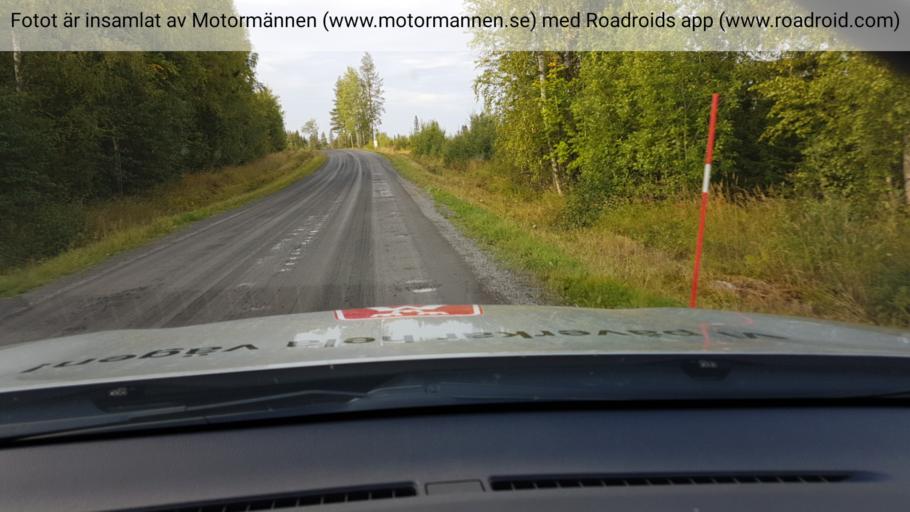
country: SE
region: Jaemtland
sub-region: Stroemsunds Kommun
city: Stroemsund
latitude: 64.1212
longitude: 15.8059
